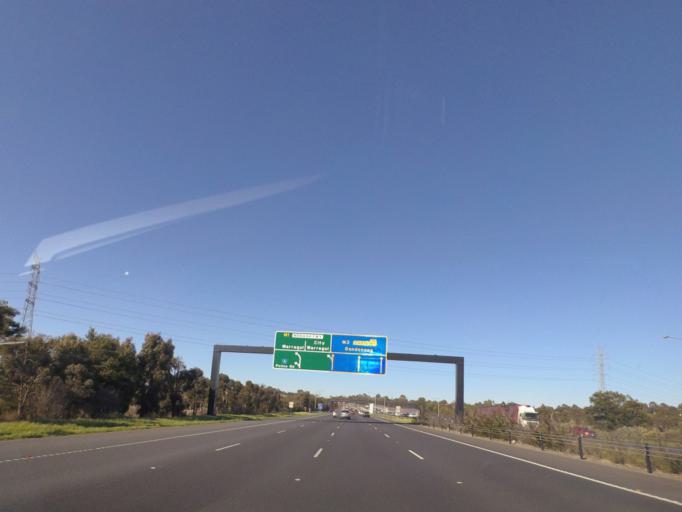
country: AU
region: Victoria
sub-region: Monash
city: Mulgrave
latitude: -37.9296
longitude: 145.2112
